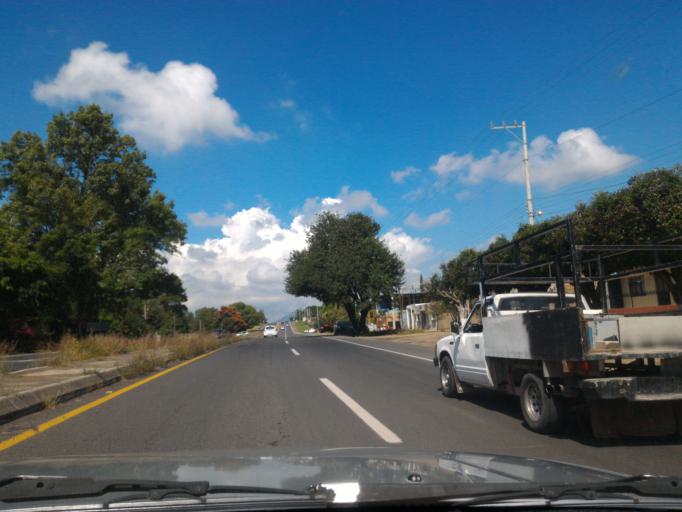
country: MX
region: Jalisco
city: Arenal
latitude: 20.7485
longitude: -103.6470
